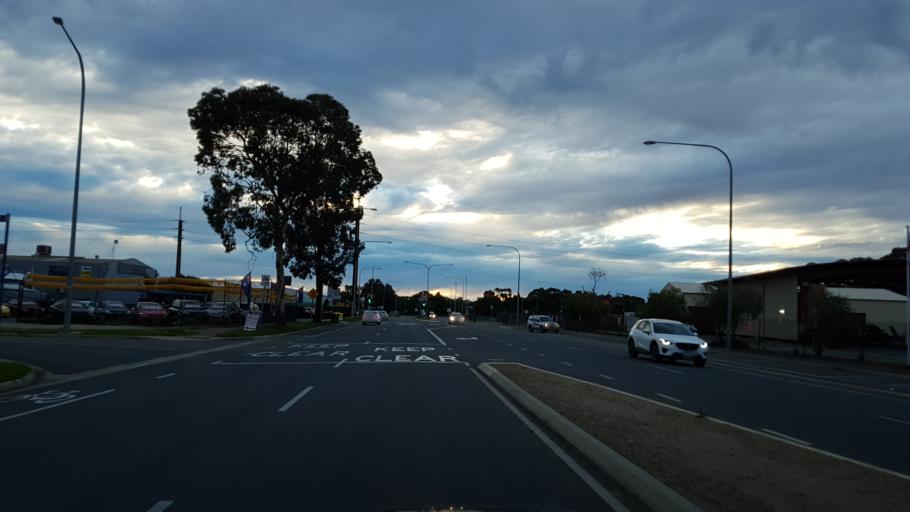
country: AU
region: South Australia
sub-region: Salisbury
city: Salisbury
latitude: -34.7517
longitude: 138.6455
